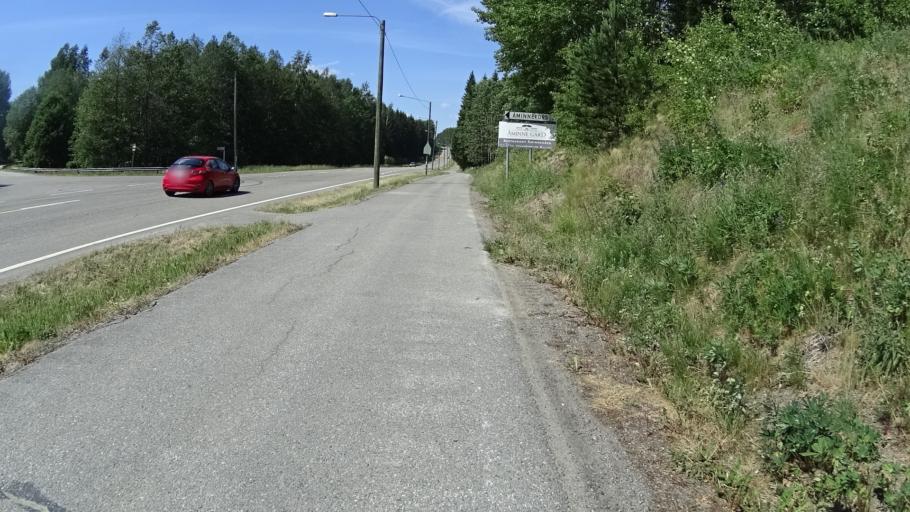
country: FI
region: Uusimaa
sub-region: Raaseporin
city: Karis
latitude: 60.0961
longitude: 23.6101
